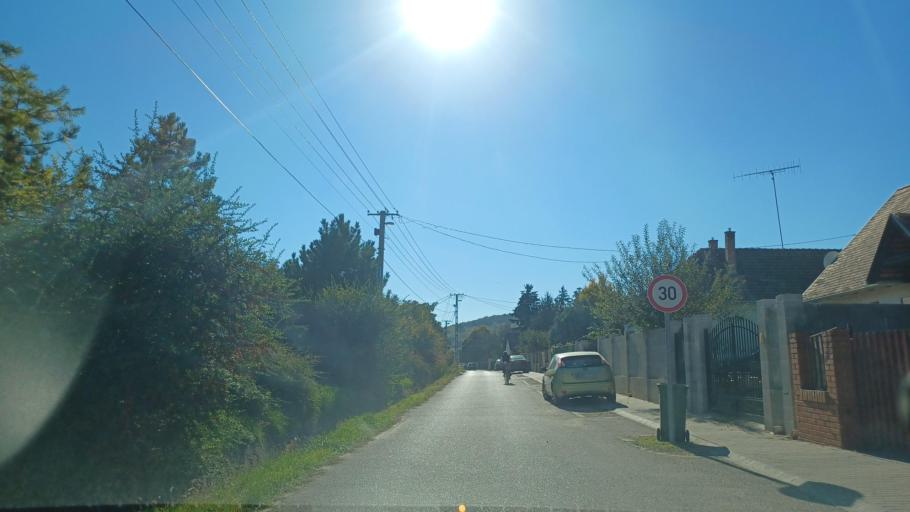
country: HU
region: Tolna
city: Szekszard
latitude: 46.3118
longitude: 18.6911
